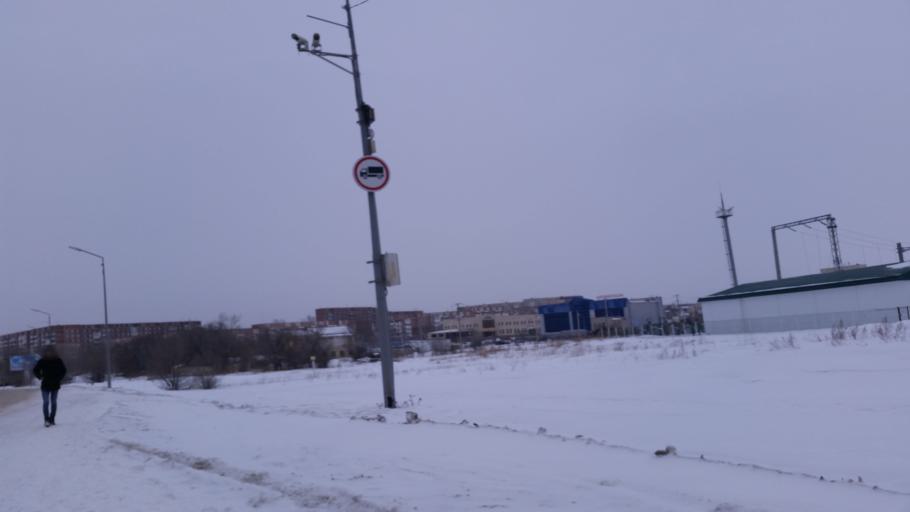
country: KZ
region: Qaraghandy
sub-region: Qaraghandy Qalasy
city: Karagandy
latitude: 49.7757
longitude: 73.1556
